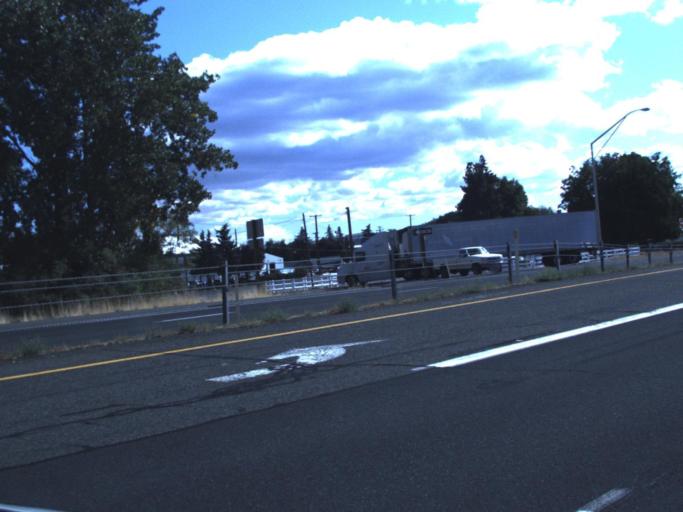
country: US
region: Washington
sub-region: Yakima County
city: Gleed
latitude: 46.6608
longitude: -120.6208
